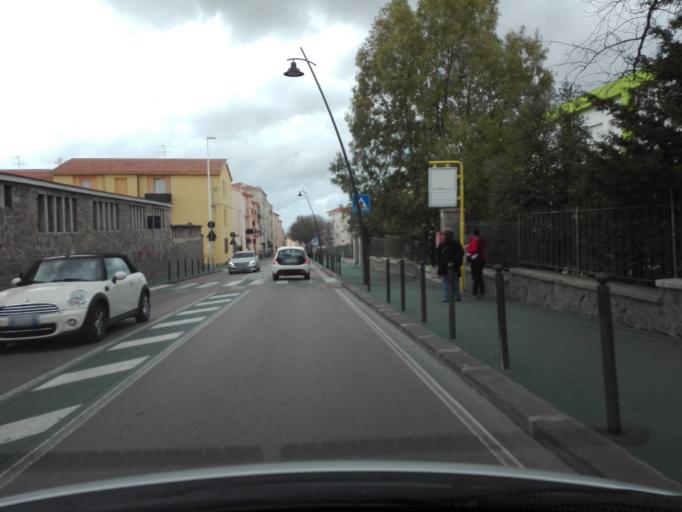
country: IT
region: Sardinia
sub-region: Provincia di Sassari
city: Sassari
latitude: 40.7352
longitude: 8.5681
